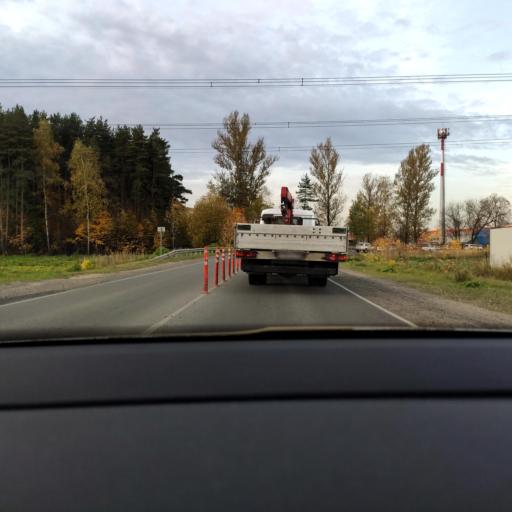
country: RU
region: Moskovskaya
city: Cherkizovo
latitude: 55.9693
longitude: 37.7648
